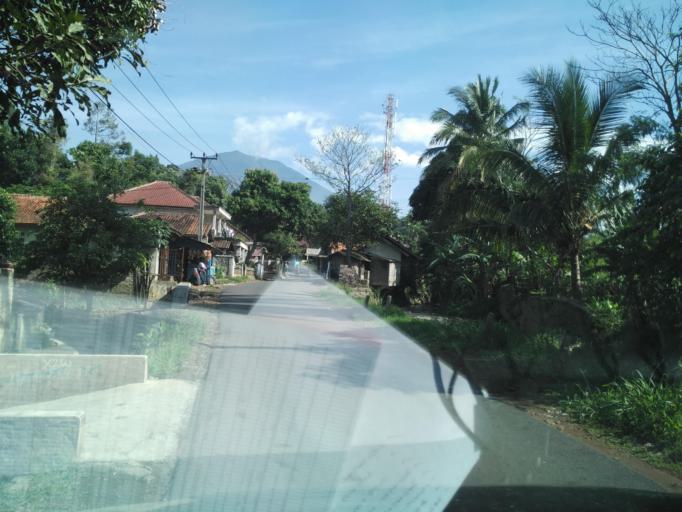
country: ID
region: West Java
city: Cibeber
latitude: -6.8582
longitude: 107.0728
